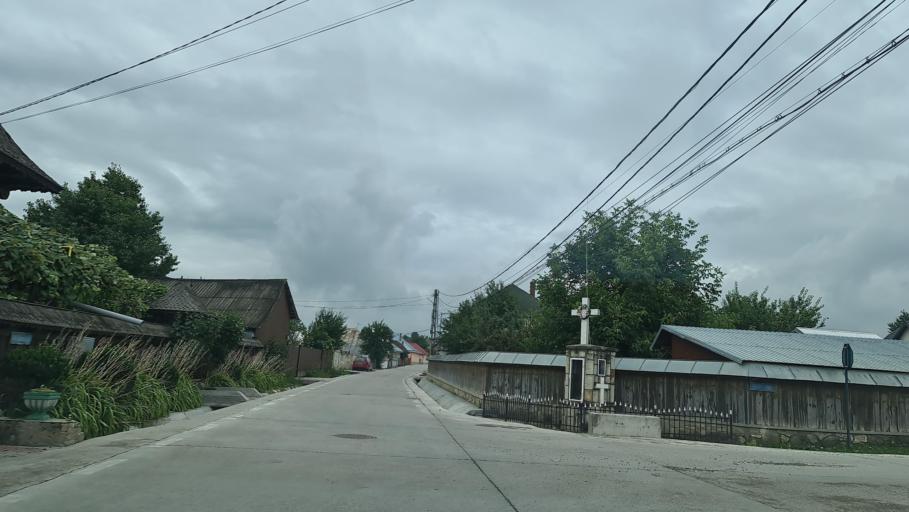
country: RO
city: Vanatori-Neamt
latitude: 47.2079
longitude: 26.3205
